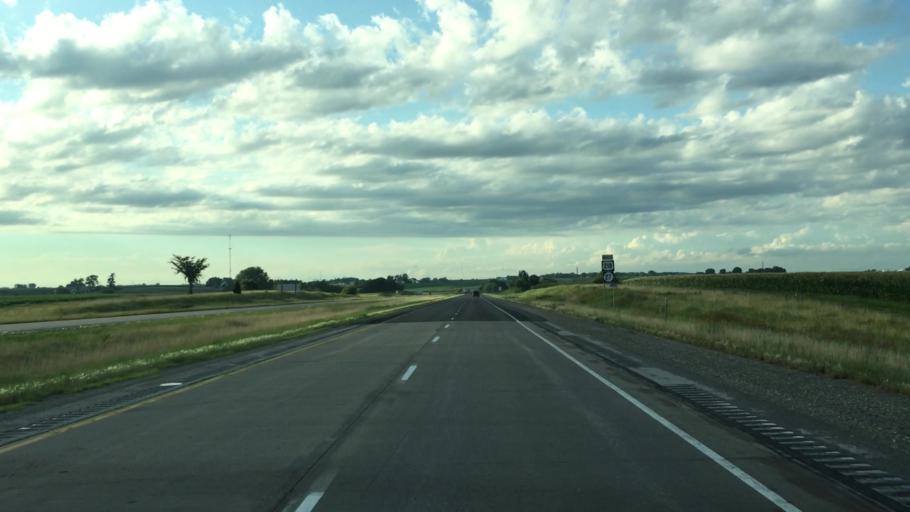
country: US
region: Iowa
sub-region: Washington County
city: Washington
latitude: 41.2957
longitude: -91.5348
